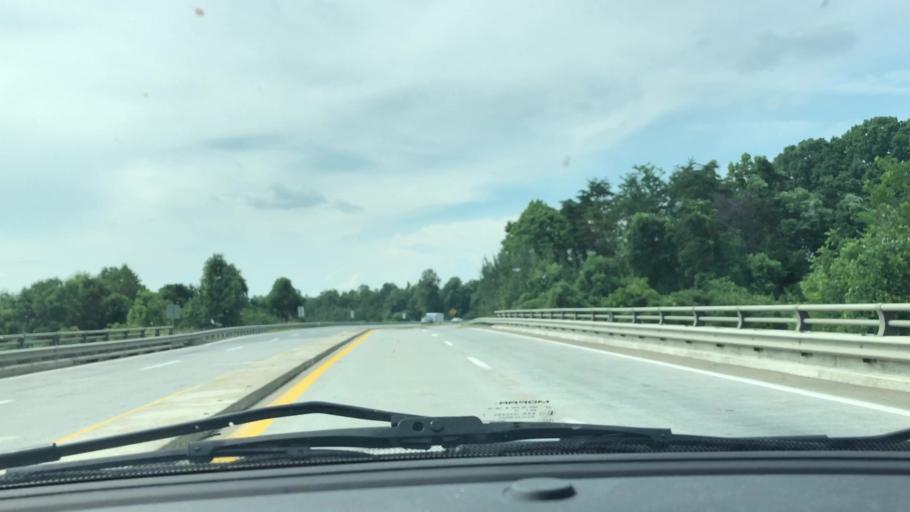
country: US
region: Virginia
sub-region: Henry County
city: Chatmoss
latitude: 36.5835
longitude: -79.8626
